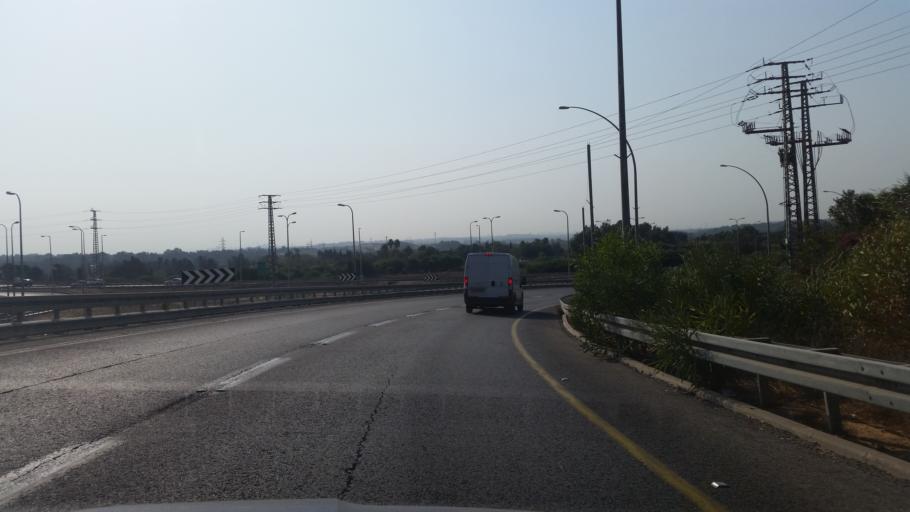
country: IL
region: Central District
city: Even Yehuda
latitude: 32.2735
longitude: 34.8536
